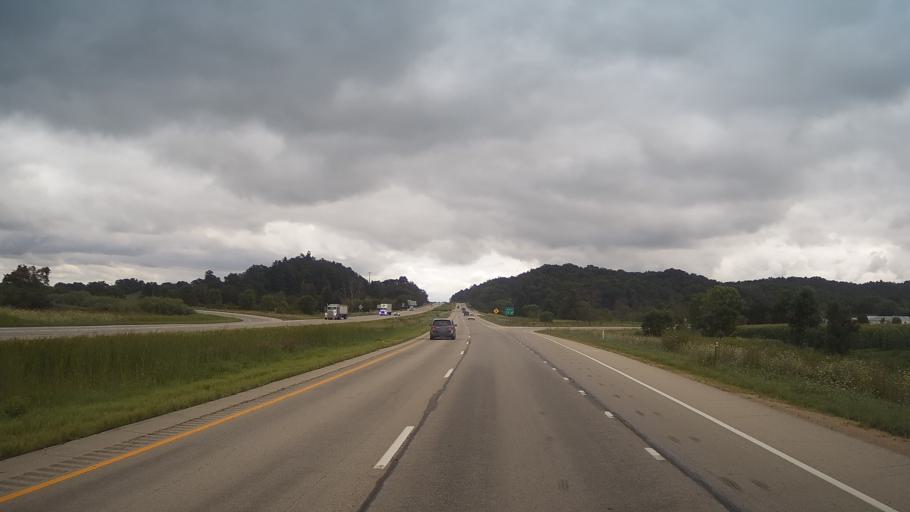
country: US
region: Wisconsin
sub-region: La Crosse County
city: Bangor
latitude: 43.8862
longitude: -91.0069
